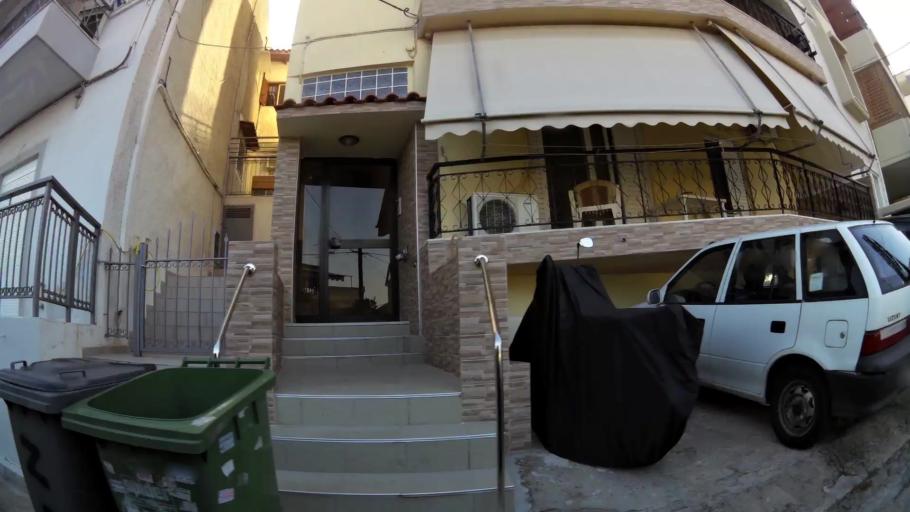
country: GR
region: Attica
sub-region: Nomos Piraios
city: Korydallos
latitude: 37.9747
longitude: 23.6341
